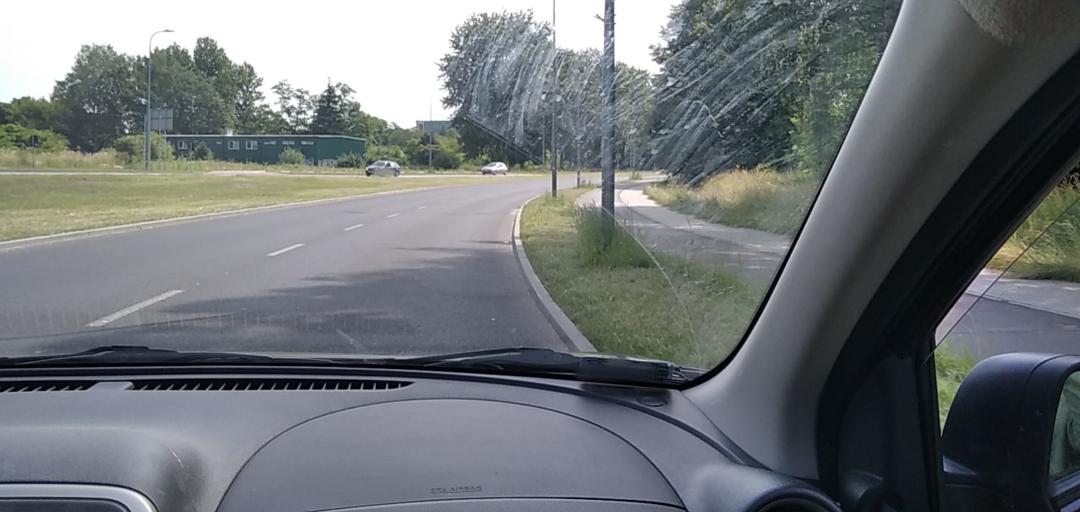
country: PL
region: Silesian Voivodeship
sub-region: Dabrowa Gornicza
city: Dabrowa Gornicza
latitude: 50.3426
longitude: 19.2337
